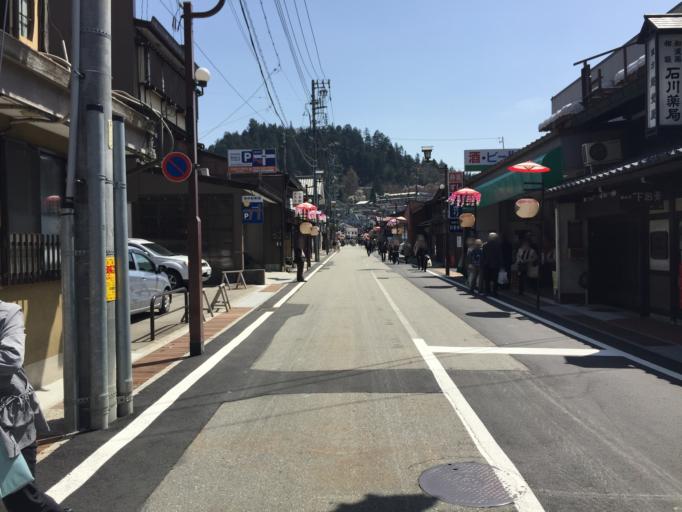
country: JP
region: Gifu
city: Takayama
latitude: 36.1437
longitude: 137.2604
